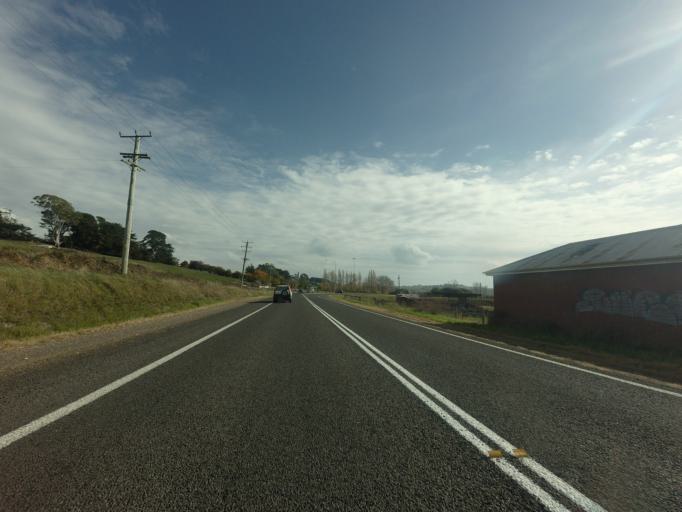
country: AU
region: Tasmania
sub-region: Meander Valley
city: Deloraine
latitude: -41.5256
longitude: 146.6857
